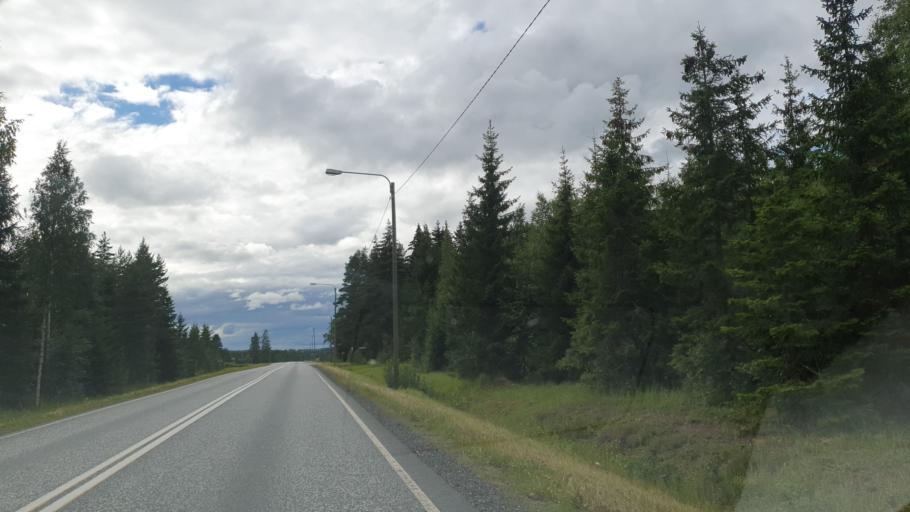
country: FI
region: Northern Savo
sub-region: Ylae-Savo
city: Iisalmi
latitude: 63.5211
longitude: 27.1746
